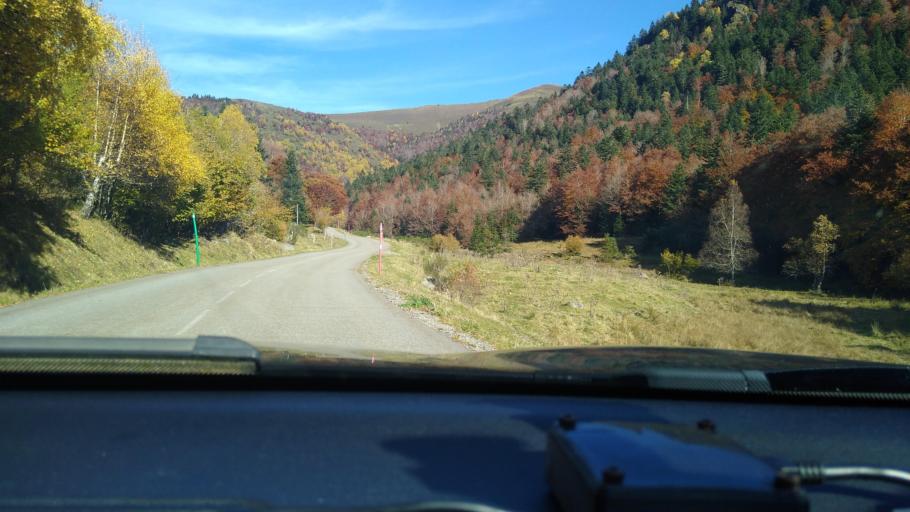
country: FR
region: Midi-Pyrenees
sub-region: Departement de l'Ariege
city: Ax-les-Thermes
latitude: 42.7265
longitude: 1.9447
